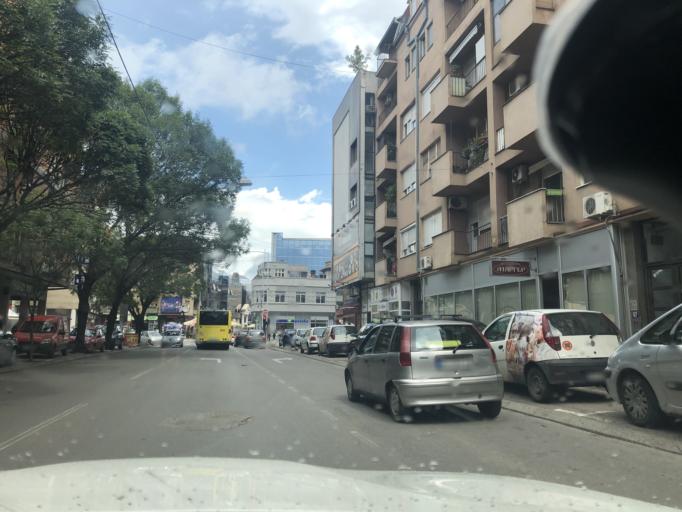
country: RS
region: Central Serbia
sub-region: Nisavski Okrug
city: Nis
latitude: 43.3162
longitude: 21.8946
